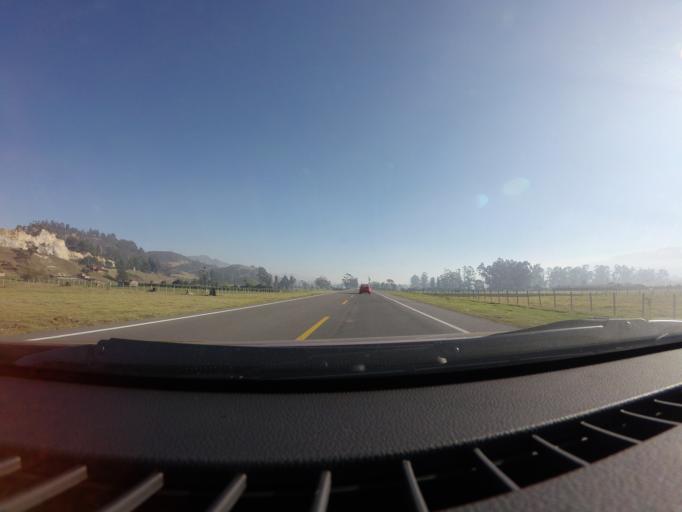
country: CO
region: Cundinamarca
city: Cogua
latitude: 5.0459
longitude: -73.9649
